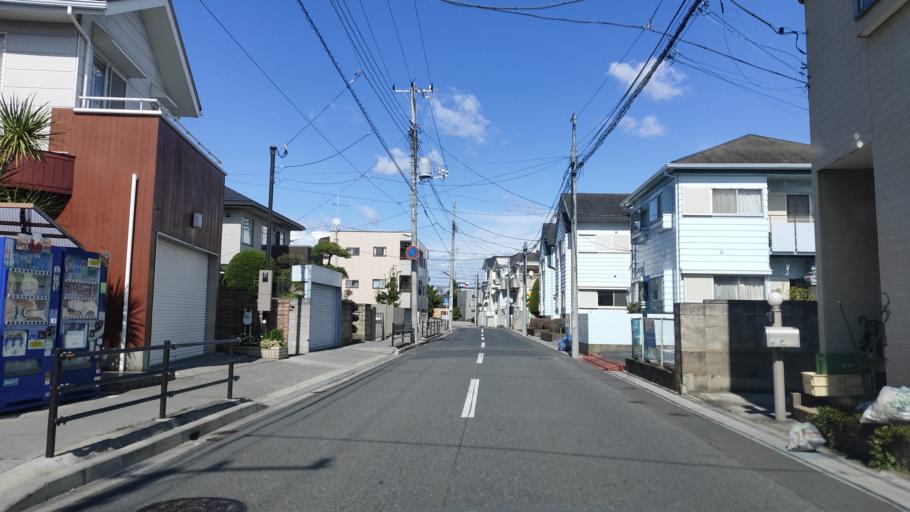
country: JP
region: Tokyo
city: Urayasu
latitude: 35.6920
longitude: 139.9196
